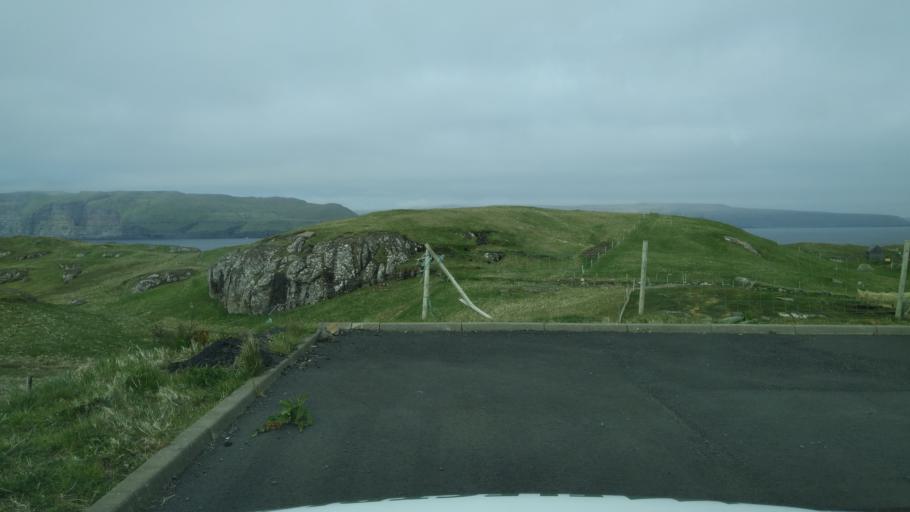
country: FO
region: Sandoy
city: Sandur
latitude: 61.9053
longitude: -6.8921
